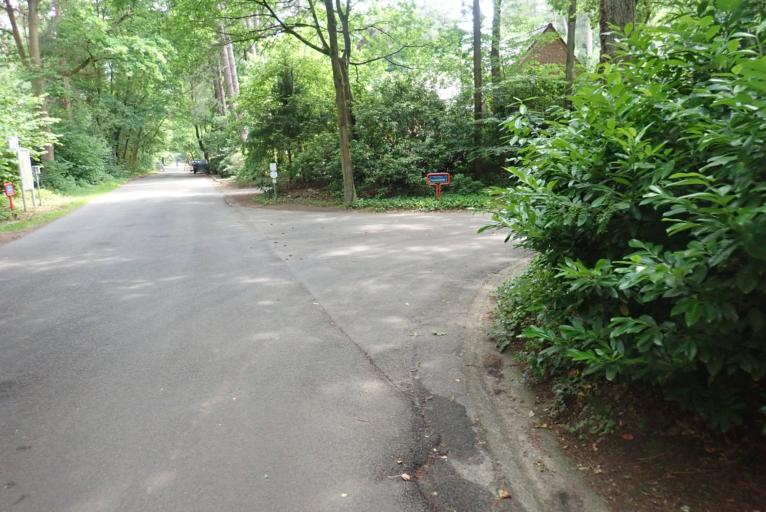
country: BE
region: Flanders
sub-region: Provincie Antwerpen
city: Kalmthout
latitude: 51.3635
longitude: 4.4808
